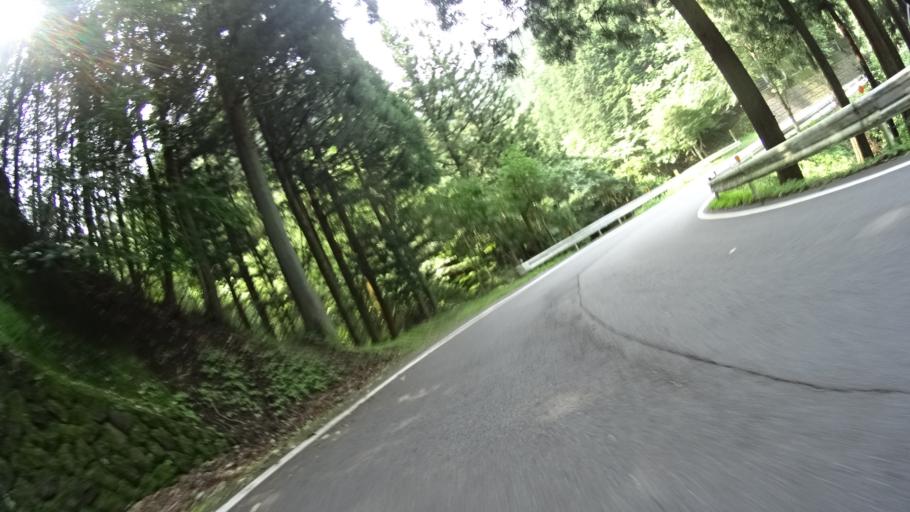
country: JP
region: Gunma
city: Tomioka
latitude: 36.0609
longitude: 138.8383
